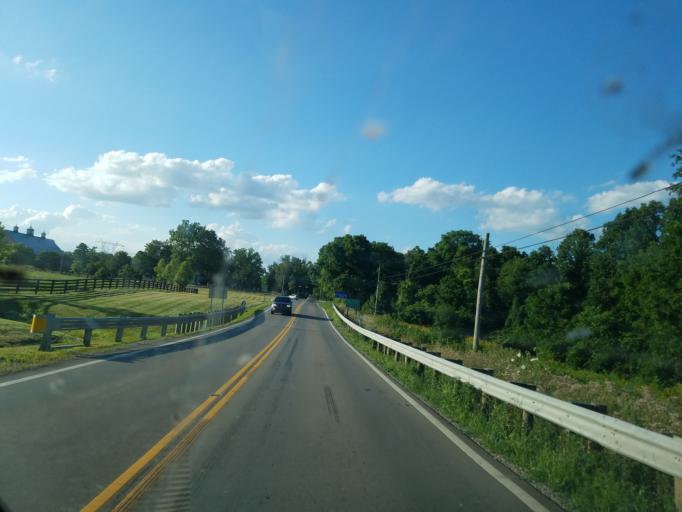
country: US
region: Ohio
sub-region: Delaware County
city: Powell
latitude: 40.1922
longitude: -83.0526
